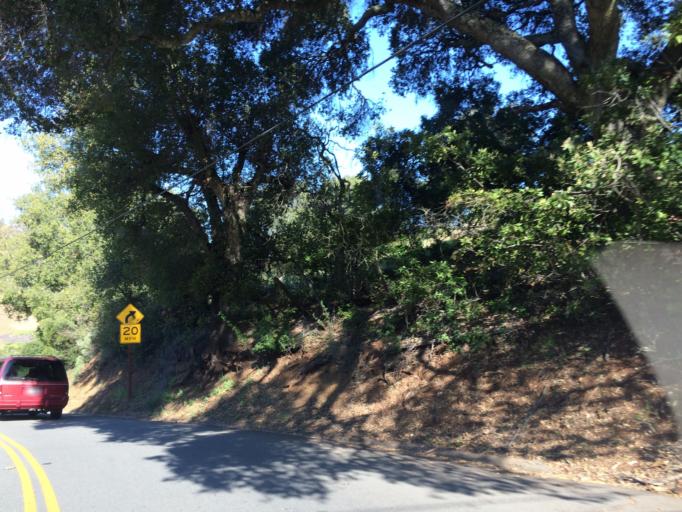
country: US
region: California
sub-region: Santa Clara County
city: Los Altos Hills
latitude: 37.3712
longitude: -122.1683
